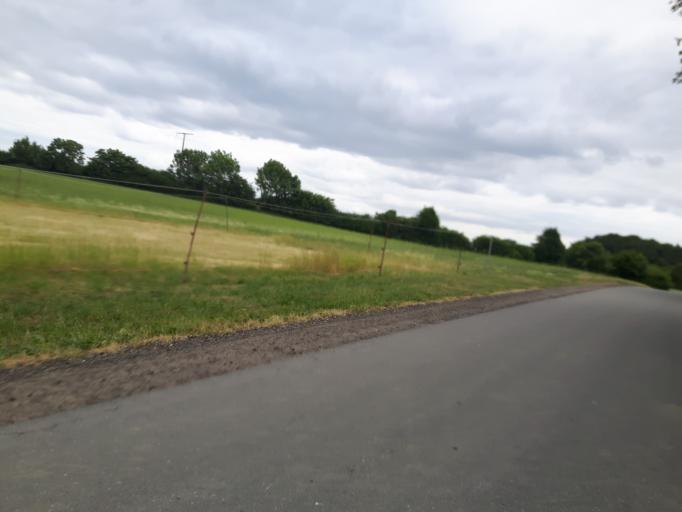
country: DE
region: Schleswig-Holstein
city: Schashagen
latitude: 54.1266
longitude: 10.9076
